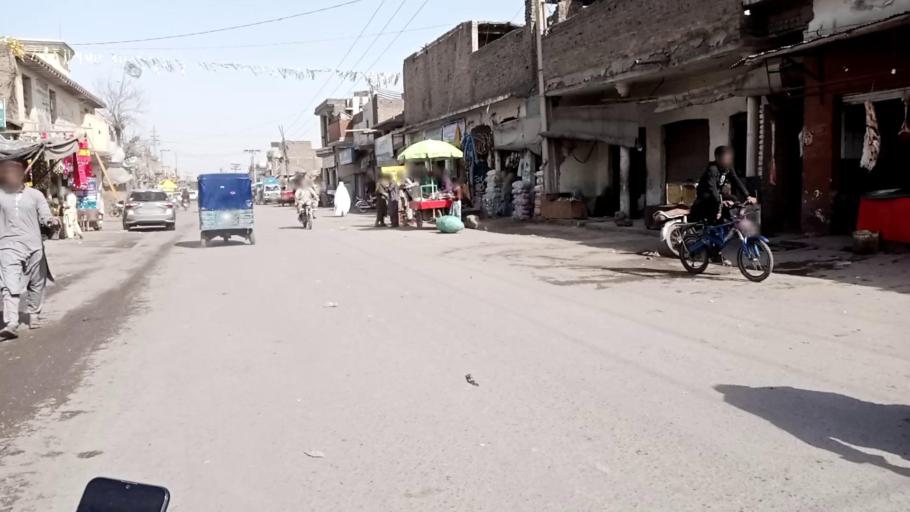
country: PK
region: Khyber Pakhtunkhwa
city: Peshawar
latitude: 33.9827
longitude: 71.6338
